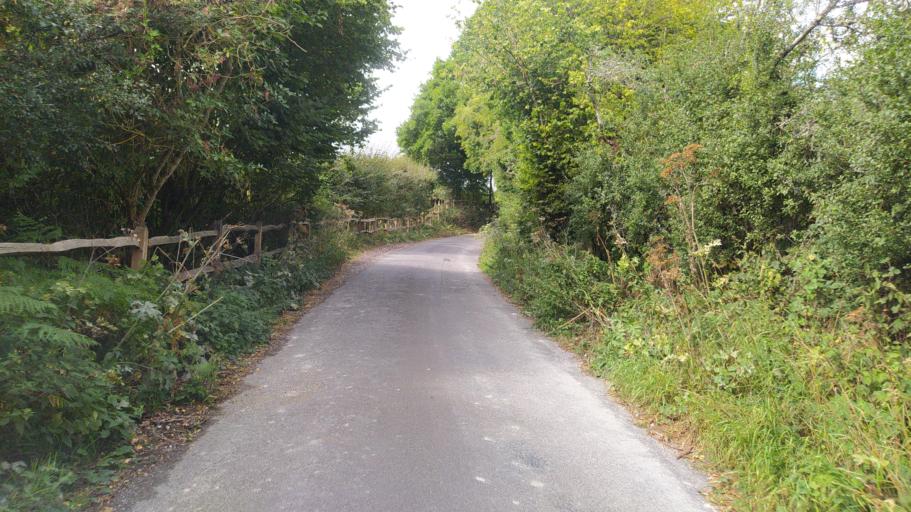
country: GB
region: England
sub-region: Hampshire
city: Petersfield
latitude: 50.9896
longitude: -0.9912
